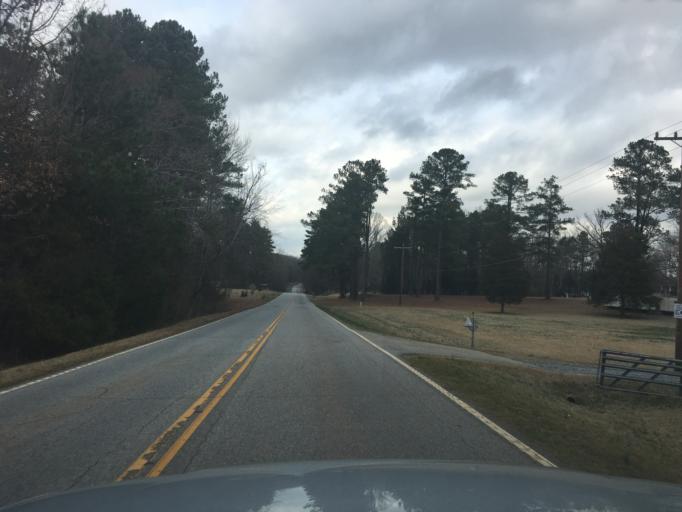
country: US
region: South Carolina
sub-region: Abbeville County
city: Abbeville
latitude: 34.2097
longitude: -82.3884
